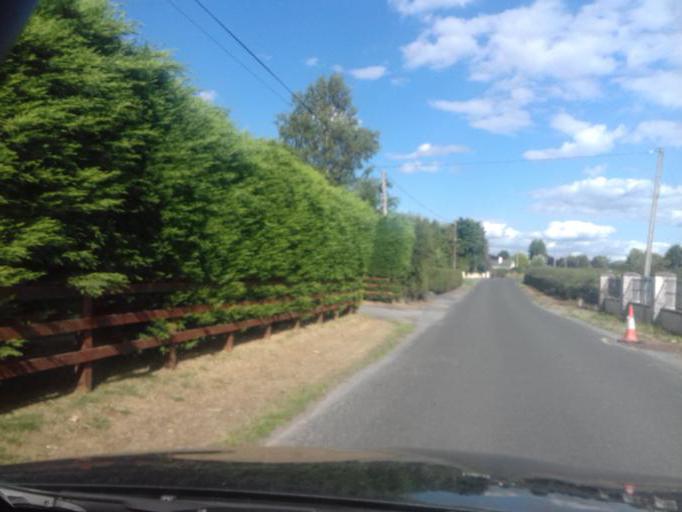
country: IE
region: Leinster
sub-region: Kilkenny
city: Thomastown
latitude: 52.5380
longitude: -7.2443
